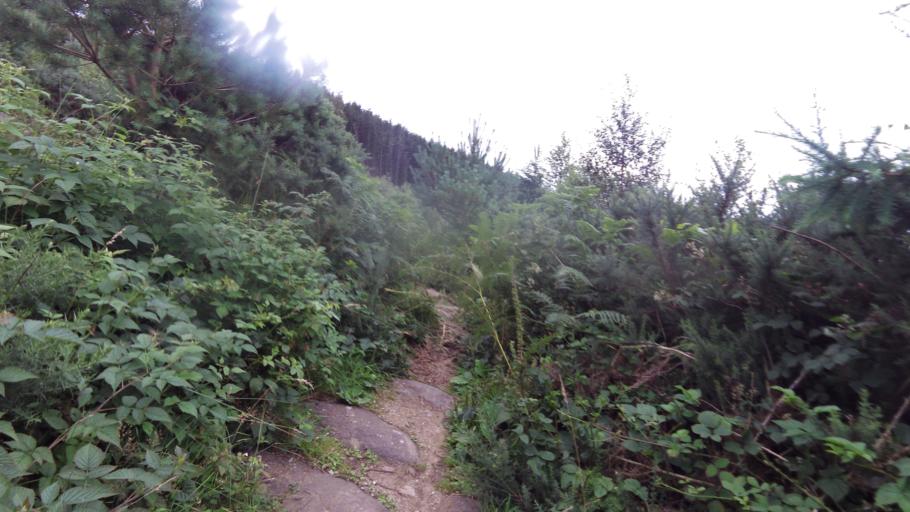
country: GB
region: England
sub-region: City and Borough of Leeds
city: Otley
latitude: 53.9542
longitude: -1.6845
